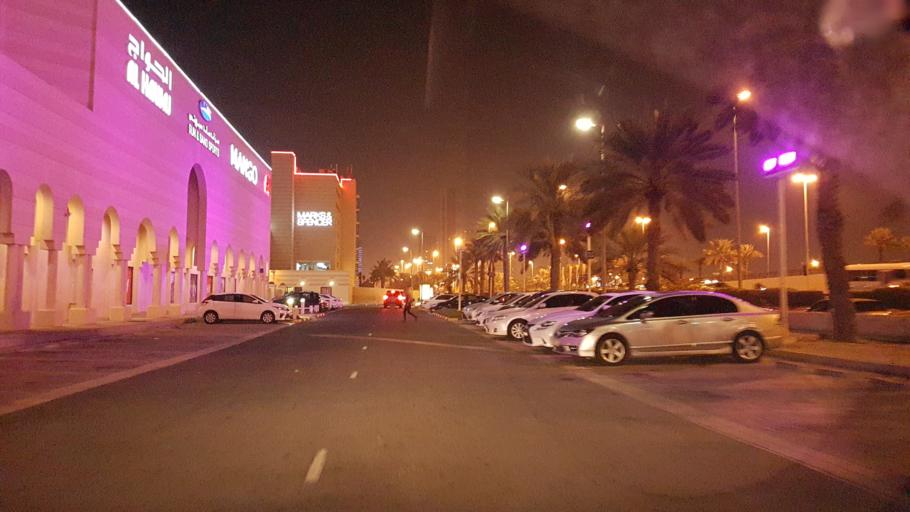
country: BH
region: Manama
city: Jidd Hafs
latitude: 26.2318
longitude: 50.5371
